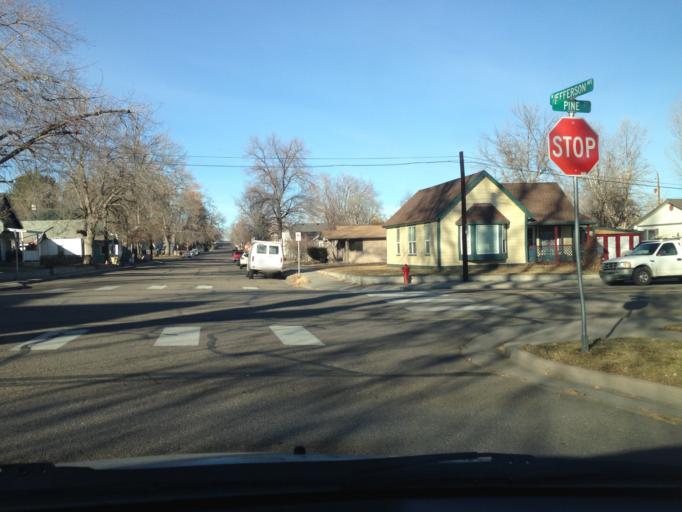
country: US
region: Colorado
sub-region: Boulder County
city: Louisville
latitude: 39.9766
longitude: -105.1346
